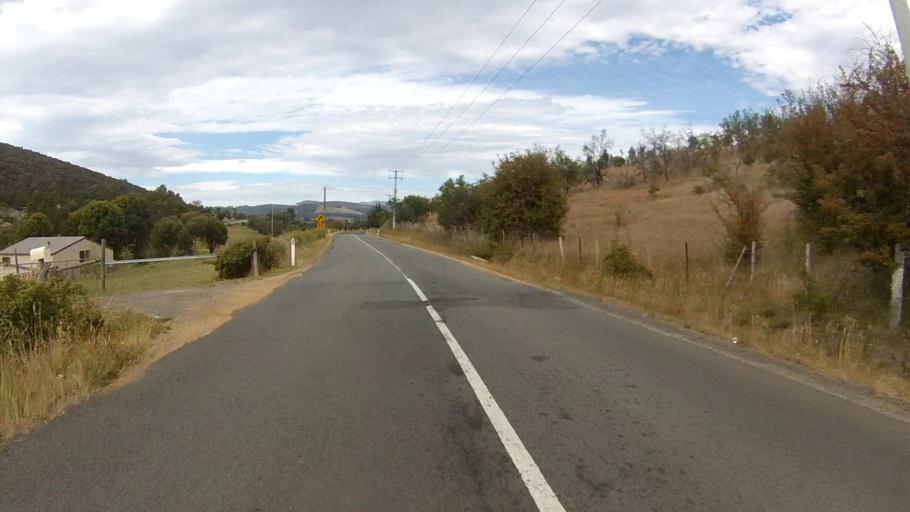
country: AU
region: Tasmania
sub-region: Clarence
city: Cambridge
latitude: -42.7388
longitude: 147.4229
